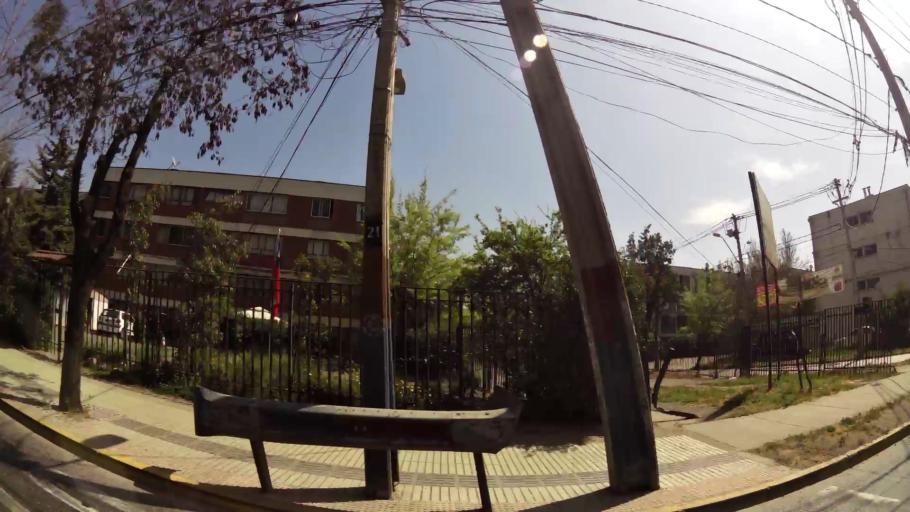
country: CL
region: Santiago Metropolitan
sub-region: Provincia de Santiago
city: Villa Presidente Frei, Nunoa, Santiago, Chile
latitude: -33.4675
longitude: -70.5508
